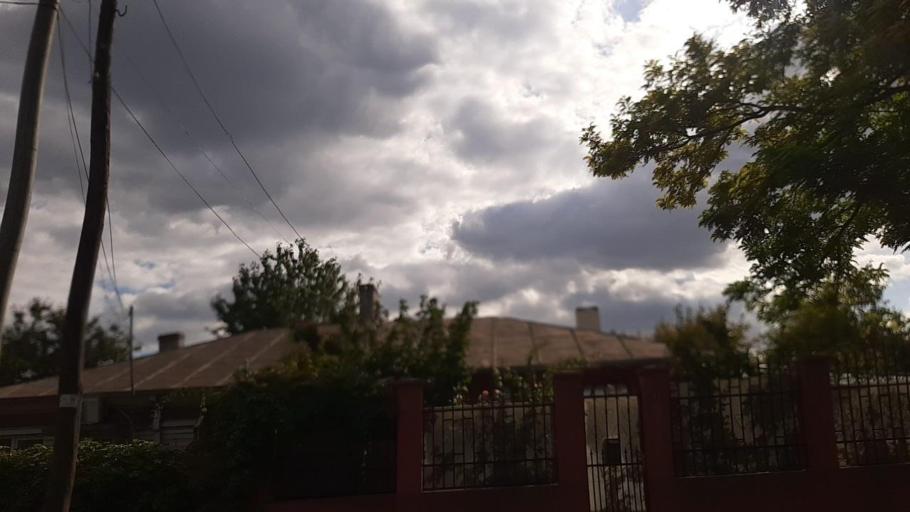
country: RO
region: Galati
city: Galati
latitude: 45.4483
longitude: 28.0326
